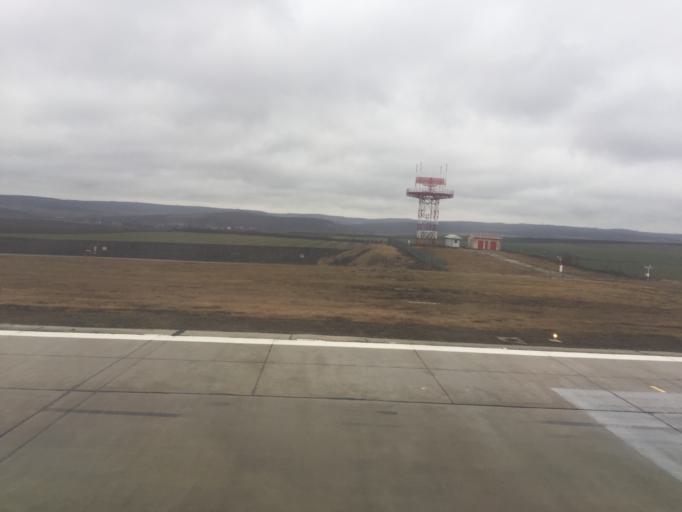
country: MD
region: Chisinau
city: Singera
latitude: 46.9278
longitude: 28.9341
